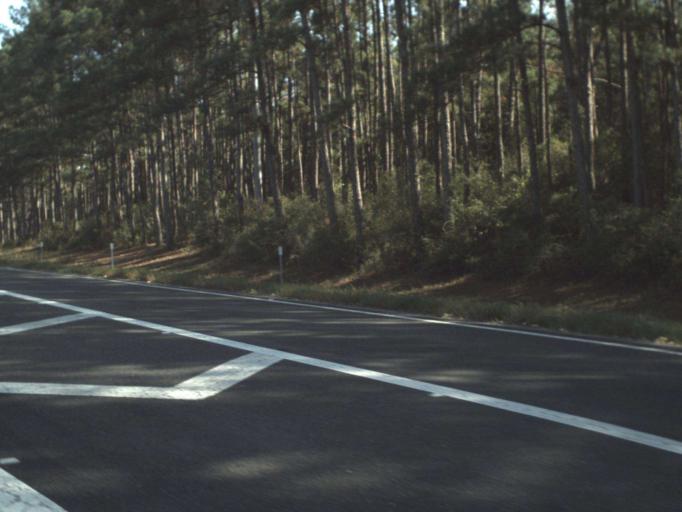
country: US
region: Florida
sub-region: Washington County
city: Chipley
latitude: 30.7486
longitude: -85.5561
